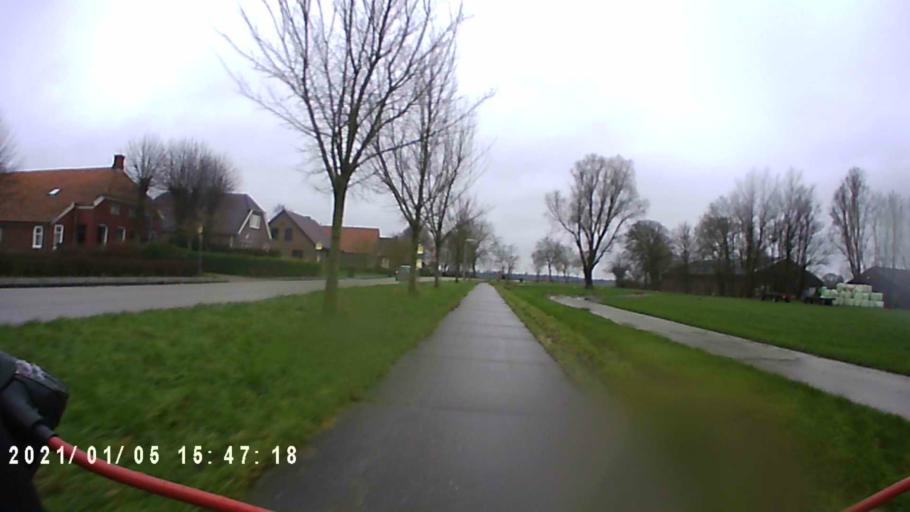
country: NL
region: Groningen
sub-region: Gemeente  Oldambt
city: Winschoten
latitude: 53.2032
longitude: 7.1152
